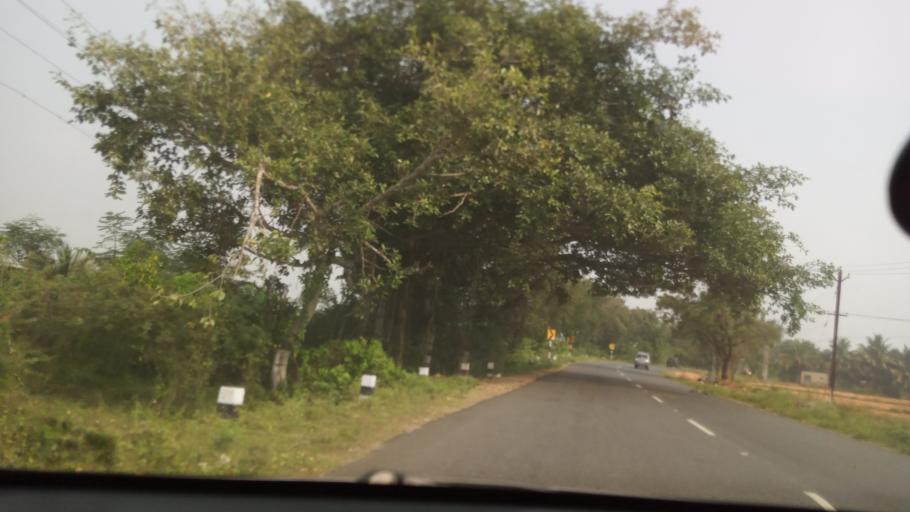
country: IN
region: Tamil Nadu
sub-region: Erode
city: Punjai Puliyampatti
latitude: 11.3242
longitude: 77.1483
